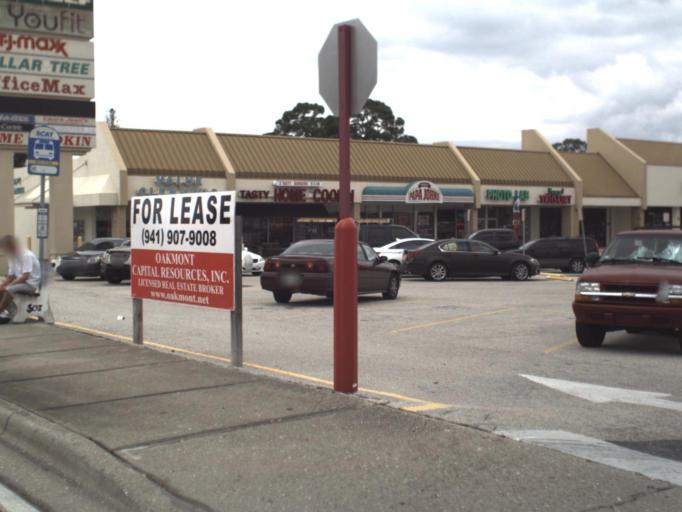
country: US
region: Florida
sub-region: Sarasota County
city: Southgate
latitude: 27.2989
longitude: -82.5154
